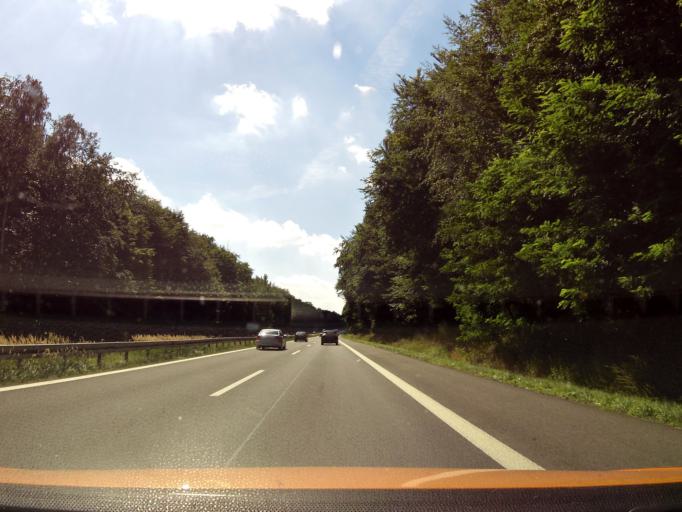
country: DE
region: Brandenburg
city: Gramzow
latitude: 53.1725
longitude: 13.9215
